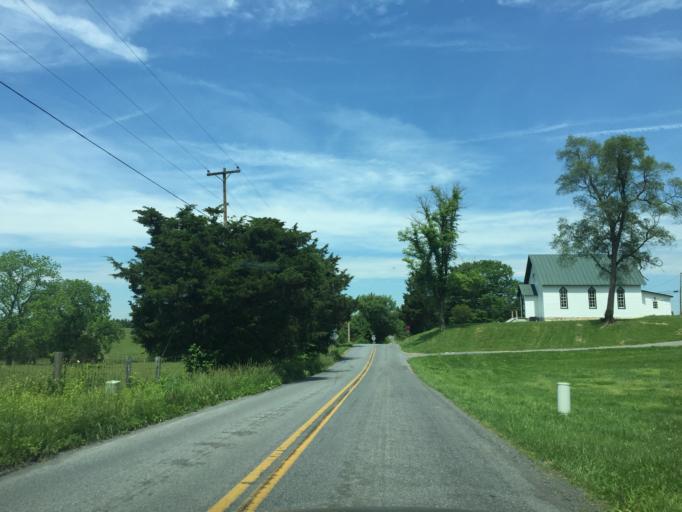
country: US
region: Virginia
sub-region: Warren County
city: Shenandoah Farms
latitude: 38.9889
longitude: -78.1406
